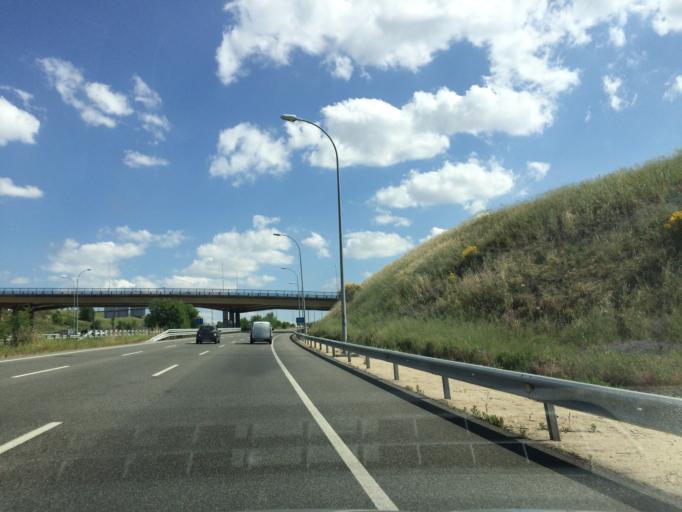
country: ES
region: Madrid
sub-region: Provincia de Madrid
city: Hortaleza
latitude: 40.4912
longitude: -3.6452
